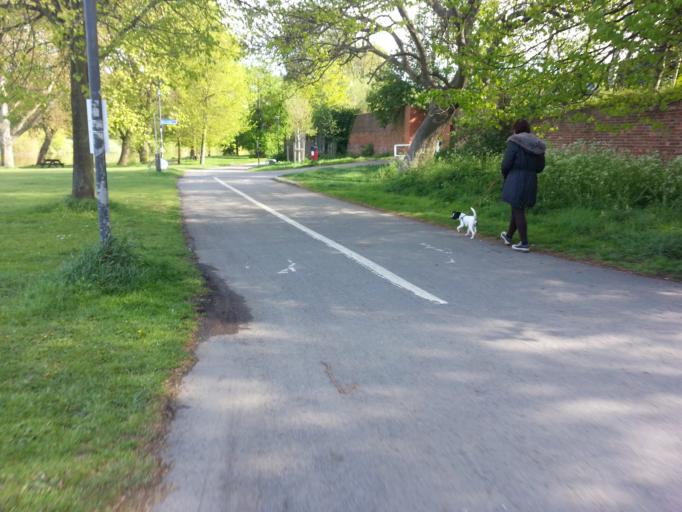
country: GB
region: England
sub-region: City of York
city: York
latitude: 53.9447
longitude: -1.0808
